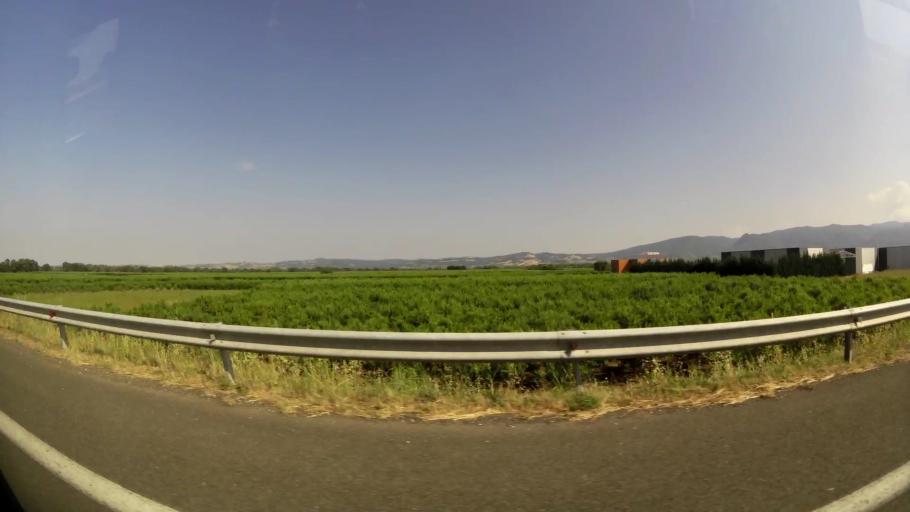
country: GR
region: Central Macedonia
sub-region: Nomos Imathias
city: Kouloura
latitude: 40.5462
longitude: 22.3274
